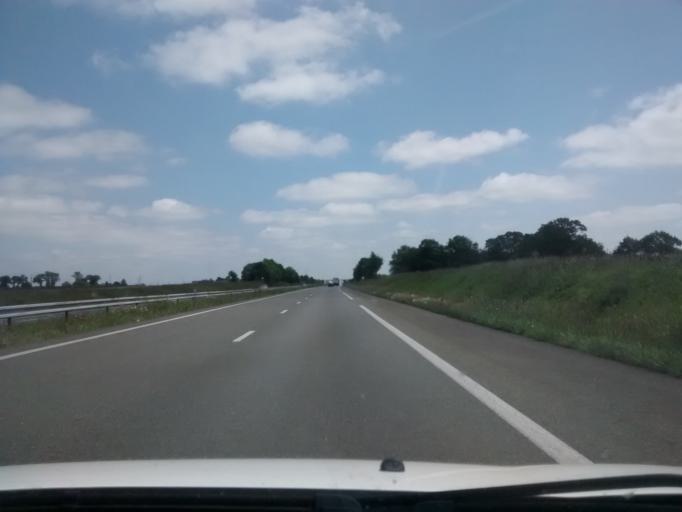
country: FR
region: Pays de la Loire
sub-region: Departement de la Mayenne
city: Soulge-sur-Ouette
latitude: 48.0724
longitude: -0.5814
